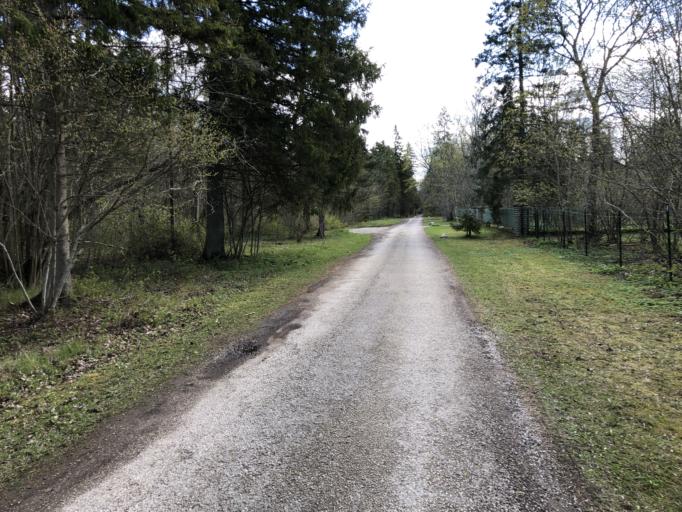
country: EE
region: Harju
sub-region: Harku vald
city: Tabasalu
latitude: 59.4390
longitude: 24.5301
